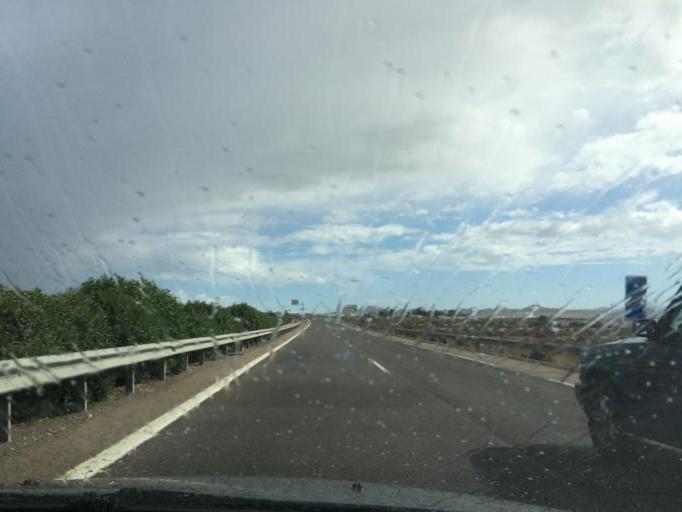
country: ES
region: Andalusia
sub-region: Provincia de Almeria
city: Retamar
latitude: 36.8664
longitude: -2.2376
